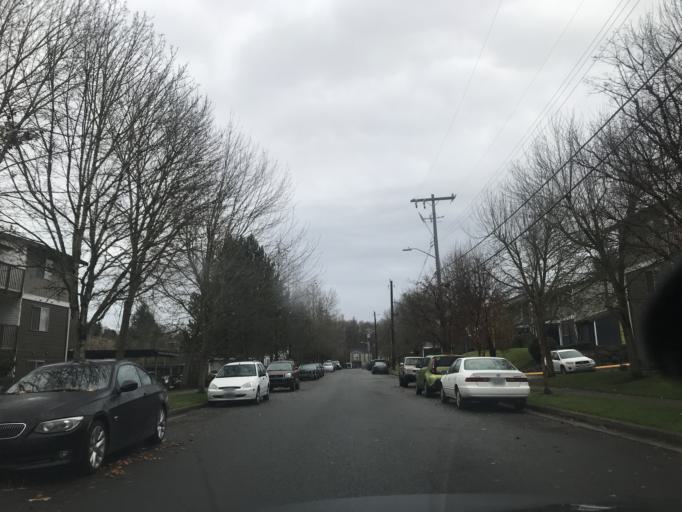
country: US
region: Washington
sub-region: King County
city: White Center
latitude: 47.5336
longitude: -122.3632
